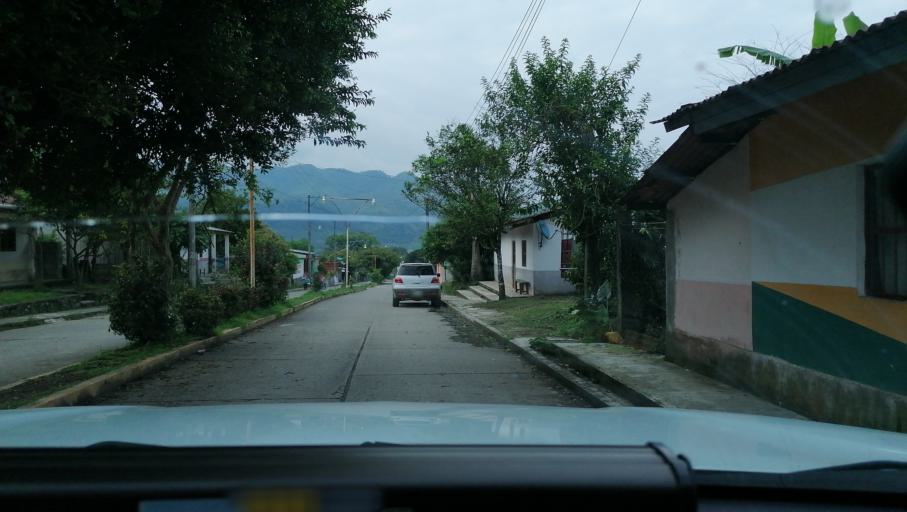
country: MX
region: Chiapas
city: Ixtacomitan
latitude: 17.3421
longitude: -93.1305
